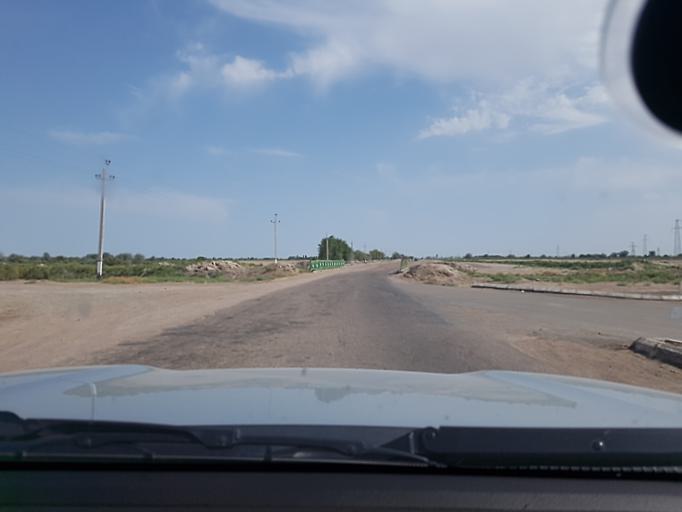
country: TM
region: Dasoguz
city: Boldumsaz
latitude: 42.1118
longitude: 59.6950
